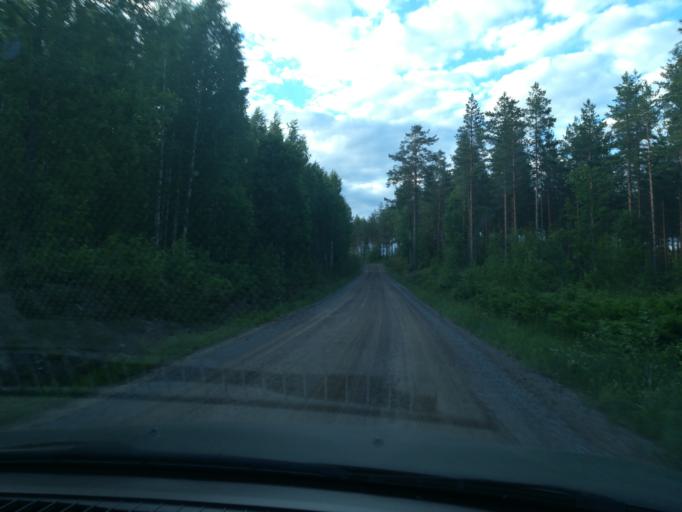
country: FI
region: Southern Savonia
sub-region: Mikkeli
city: Puumala
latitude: 61.5831
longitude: 28.1663
